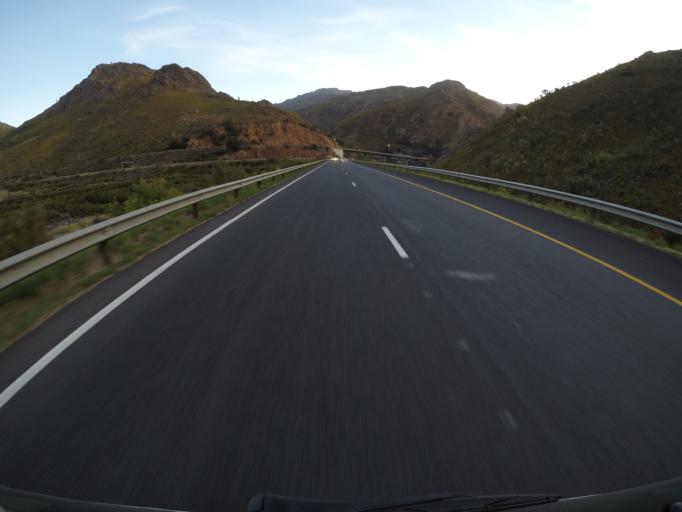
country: ZA
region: Western Cape
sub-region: Cape Winelands District Municipality
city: Paarl
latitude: -33.7293
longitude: 19.1189
